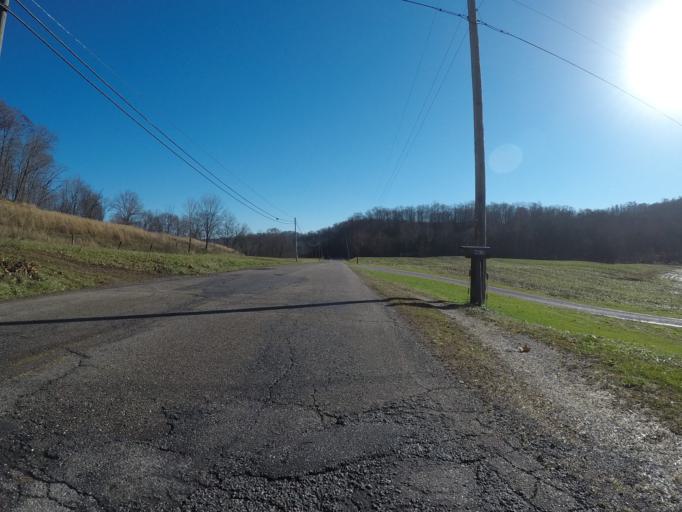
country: US
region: West Virginia
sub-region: Cabell County
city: Huntington
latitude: 38.4810
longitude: -82.4718
